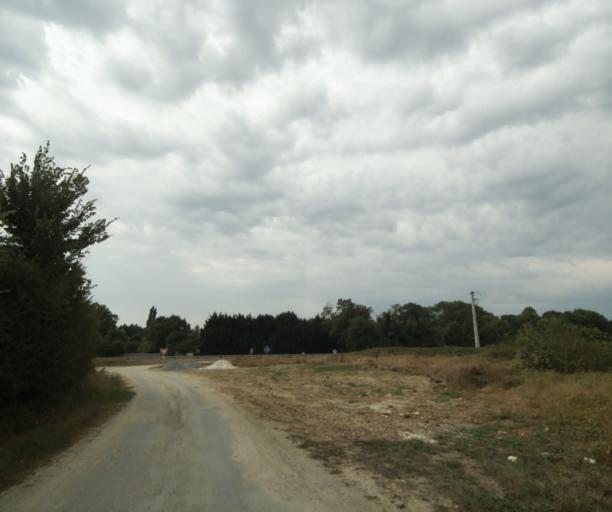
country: FR
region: Poitou-Charentes
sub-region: Departement de la Charente-Maritime
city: Tonnay-Charente
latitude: 45.9528
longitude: -0.8722
